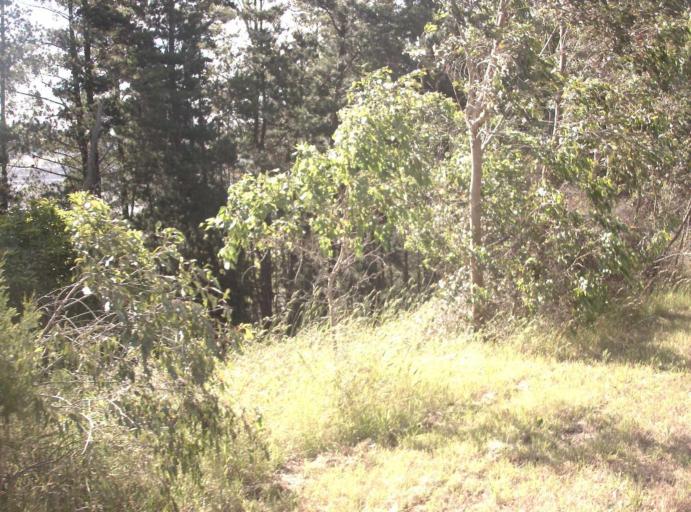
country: AU
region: Victoria
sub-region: Latrobe
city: Morwell
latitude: -38.1845
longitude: 146.4043
